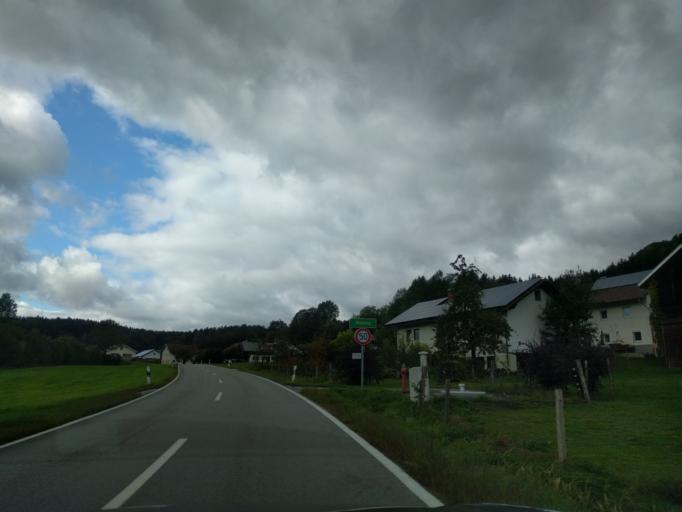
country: DE
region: Bavaria
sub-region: Lower Bavaria
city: Lalling
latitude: 48.8352
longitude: 13.1100
